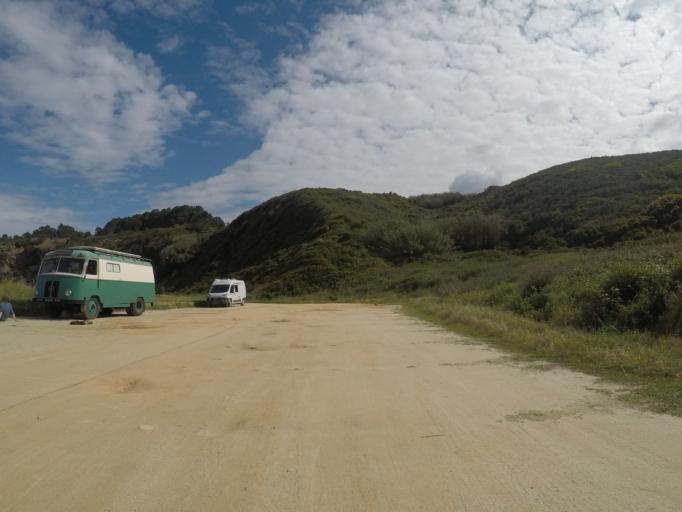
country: PT
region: Beja
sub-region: Odemira
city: Sao Teotonio
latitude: 37.4412
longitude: -8.7950
